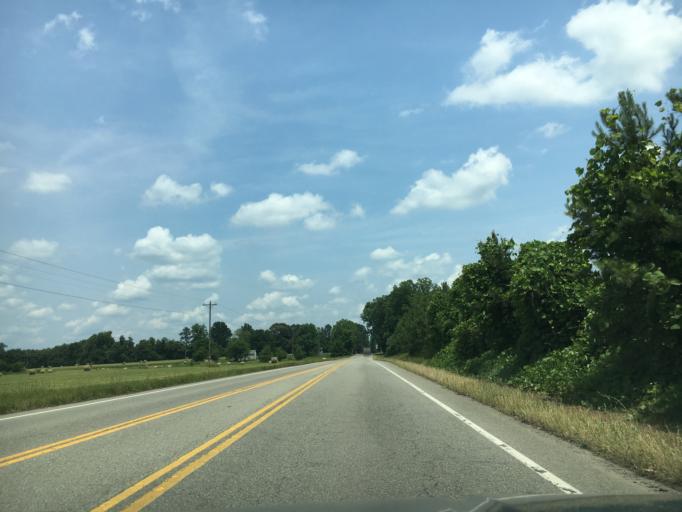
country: US
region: Virginia
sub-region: Cumberland County
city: Cumberland
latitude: 37.5487
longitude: -78.0954
